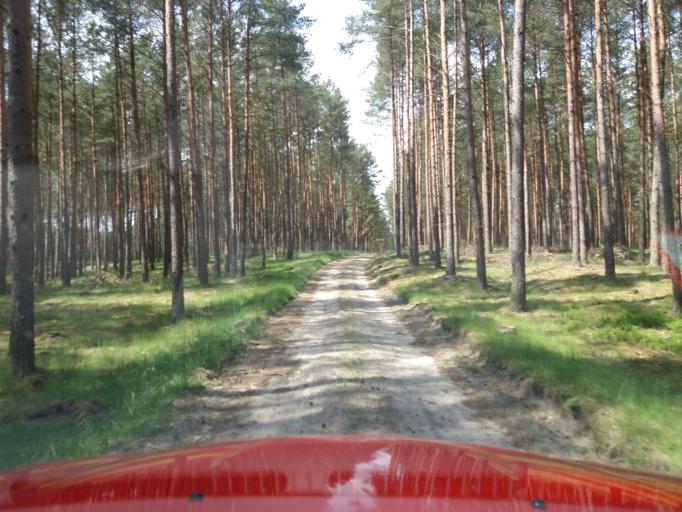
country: PL
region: West Pomeranian Voivodeship
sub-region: Powiat choszczenski
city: Drawno
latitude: 53.1468
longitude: 15.7620
